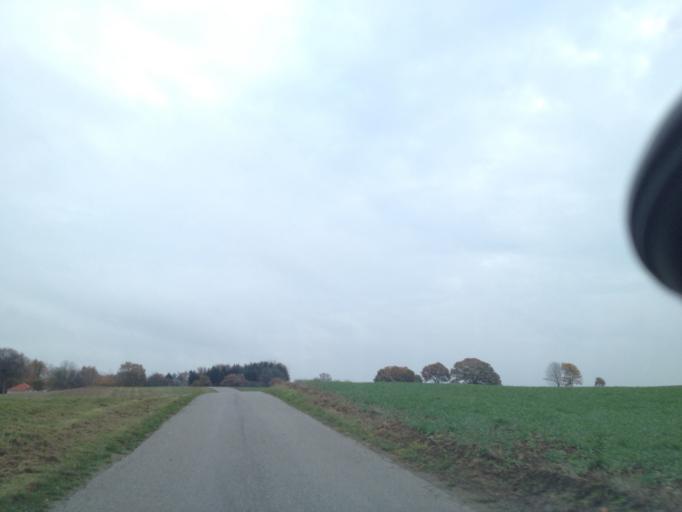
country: DK
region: South Denmark
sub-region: Nordfyns Kommune
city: Sonderso
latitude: 55.4242
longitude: 10.2114
